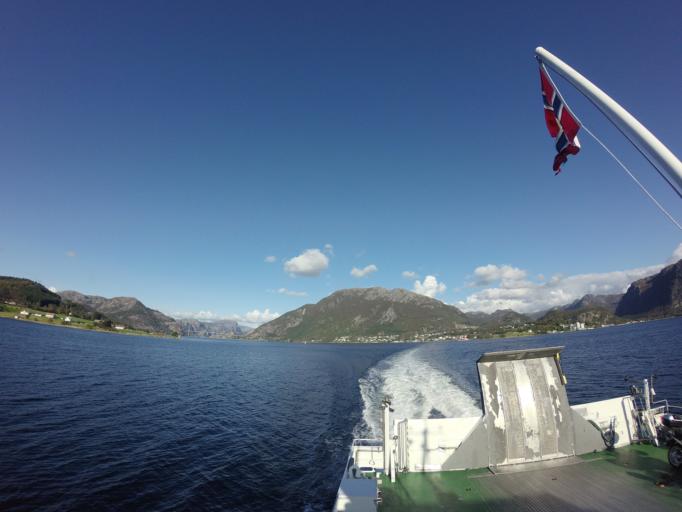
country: NO
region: Rogaland
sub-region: Forsand
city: Forsand
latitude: 58.8995
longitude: 6.0706
